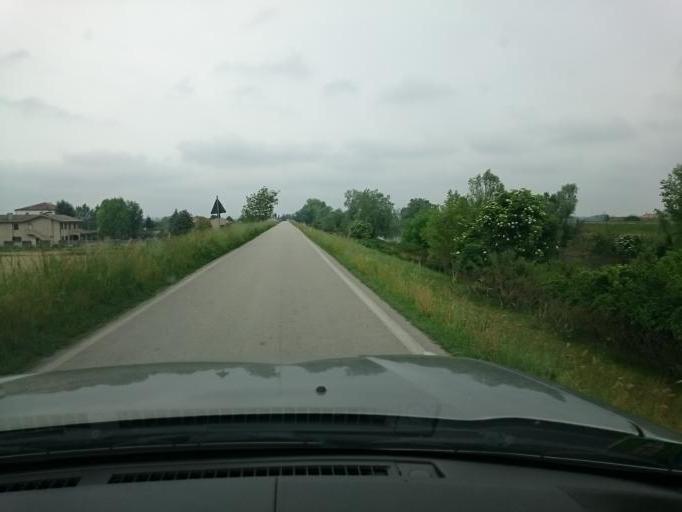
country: IT
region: Veneto
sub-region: Provincia di Padova
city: Campagnola
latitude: 45.2588
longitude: 11.9829
